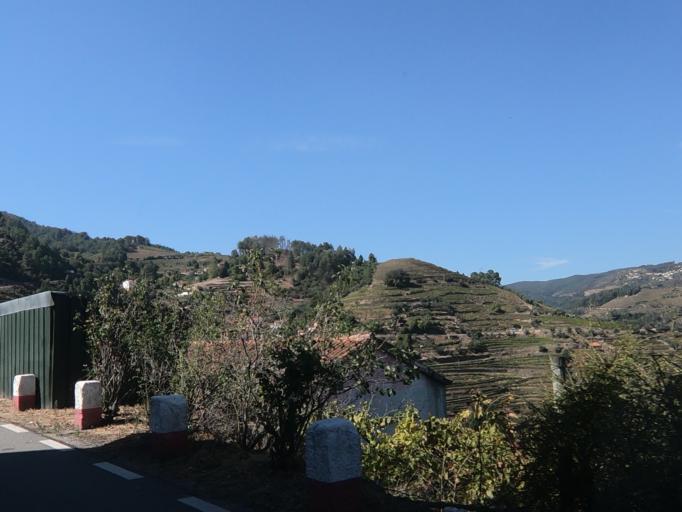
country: PT
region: Vila Real
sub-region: Santa Marta de Penaguiao
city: Santa Marta de Penaguiao
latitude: 41.2292
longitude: -7.7871
